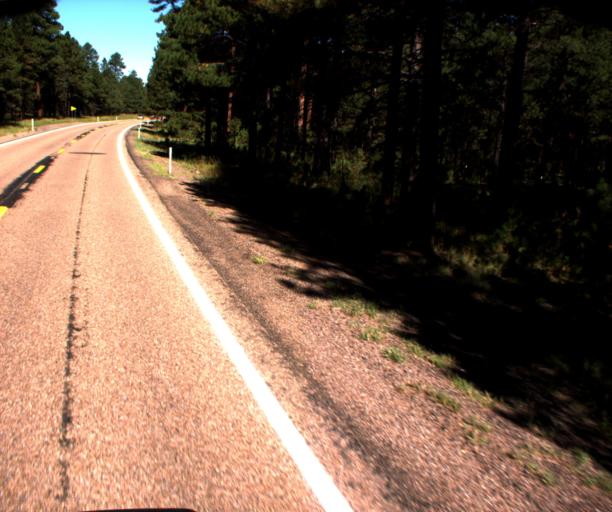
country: US
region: Arizona
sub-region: Navajo County
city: Pinetop-Lakeside
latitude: 34.0459
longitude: -109.7132
